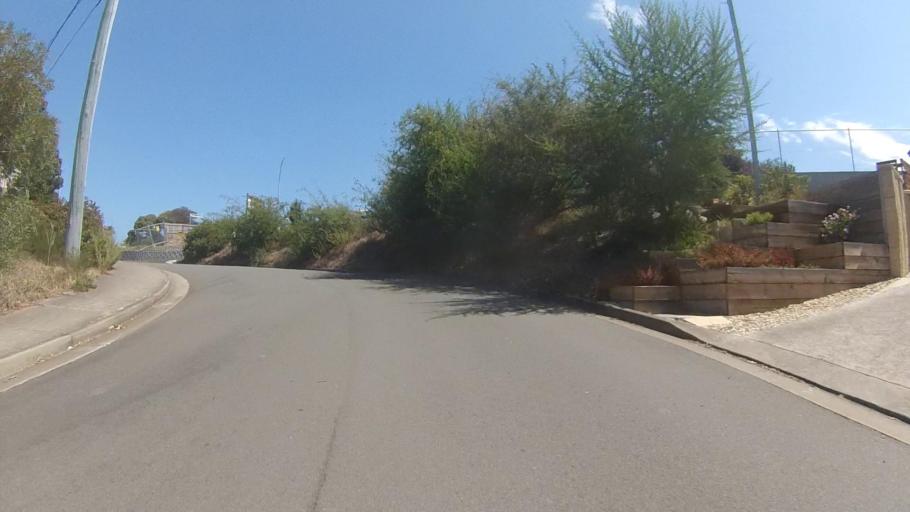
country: AU
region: Tasmania
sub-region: Sorell
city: Sorell
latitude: -42.7986
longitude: 147.5338
